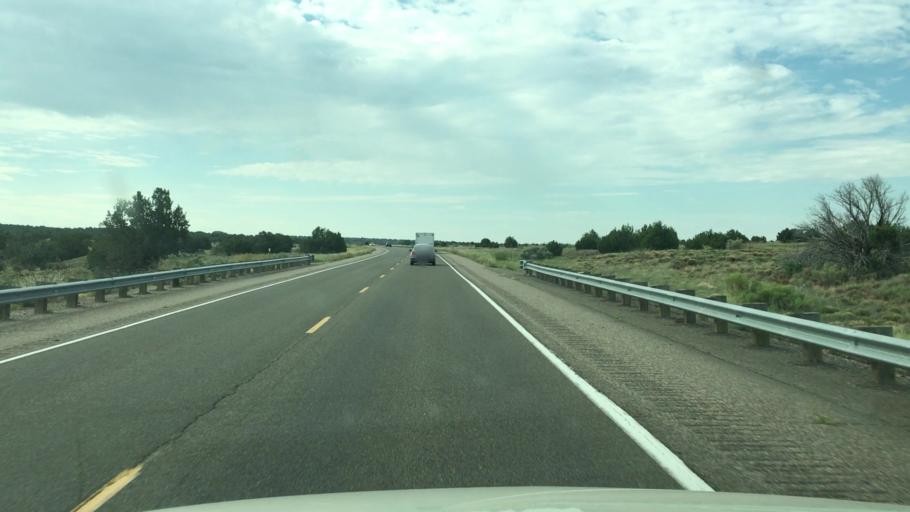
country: US
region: New Mexico
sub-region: Santa Fe County
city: Eldorado at Santa Fe
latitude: 35.2955
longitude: -105.8261
